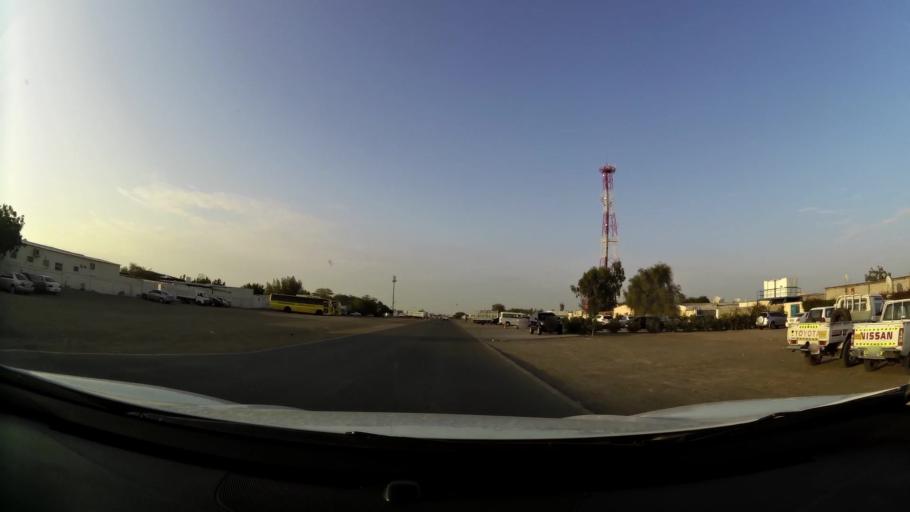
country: AE
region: Abu Dhabi
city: Al Ain
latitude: 24.1503
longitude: 55.8131
